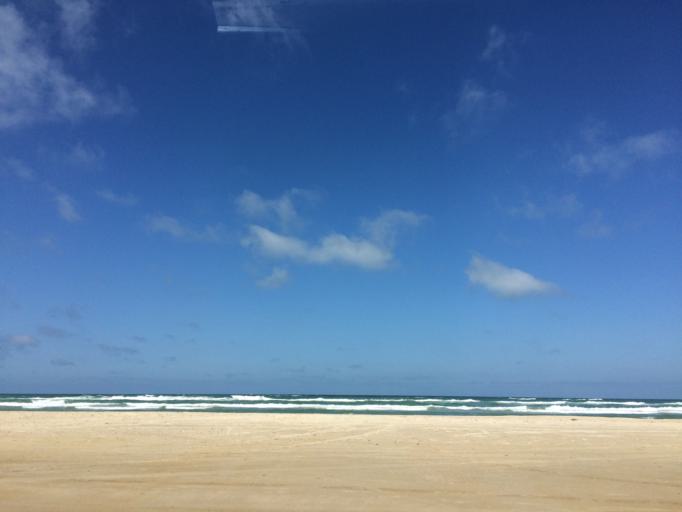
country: DK
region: North Denmark
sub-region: Jammerbugt Kommune
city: Brovst
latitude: 57.2240
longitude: 9.5373
